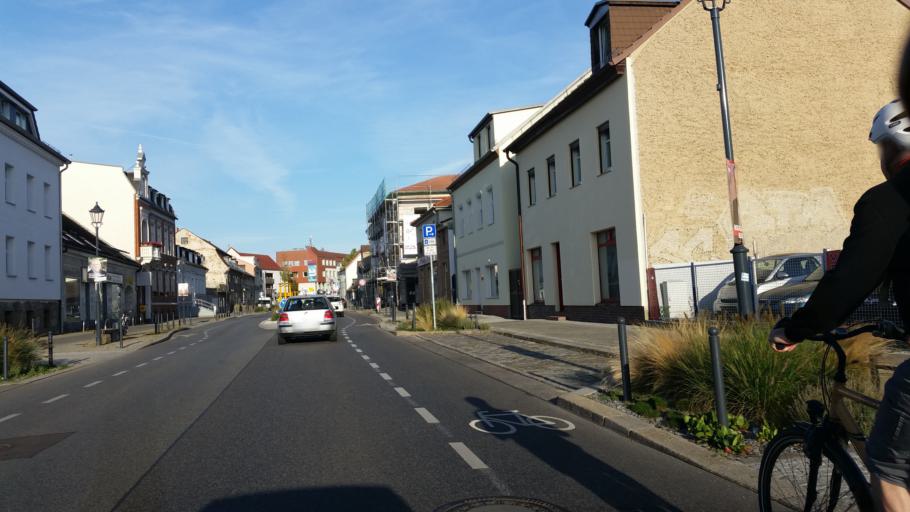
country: DE
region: Brandenburg
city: Teltow
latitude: 52.4011
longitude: 13.2639
